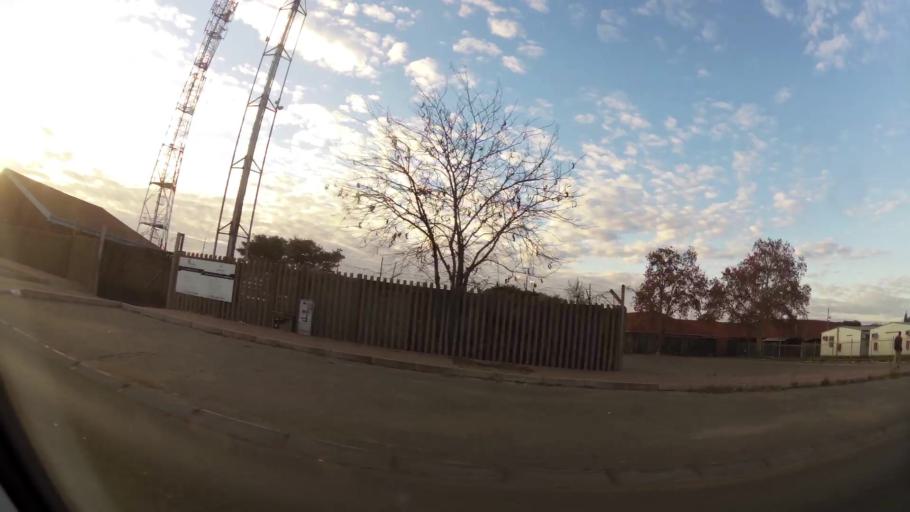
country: ZA
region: Gauteng
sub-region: City of Tshwane Metropolitan Municipality
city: Pretoria
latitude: -25.7147
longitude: 28.3467
